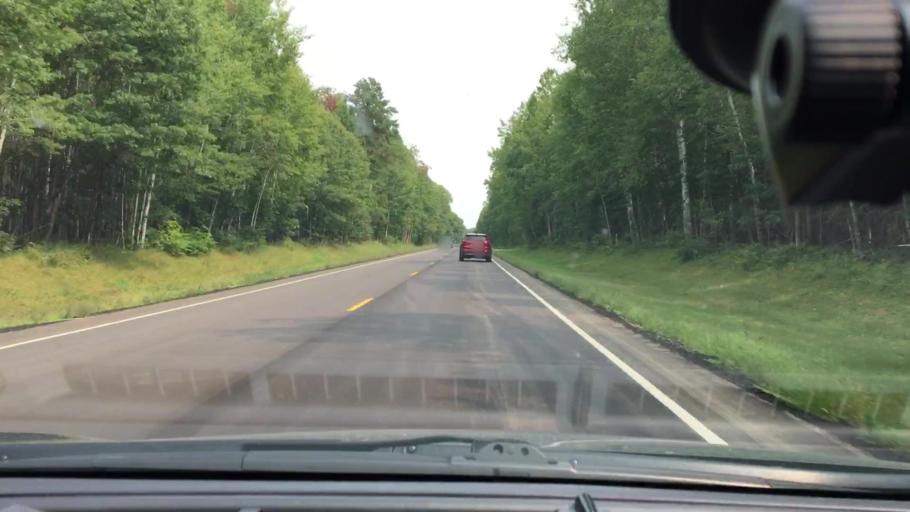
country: US
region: Minnesota
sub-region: Crow Wing County
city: Breezy Point
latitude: 46.5335
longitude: -94.1734
